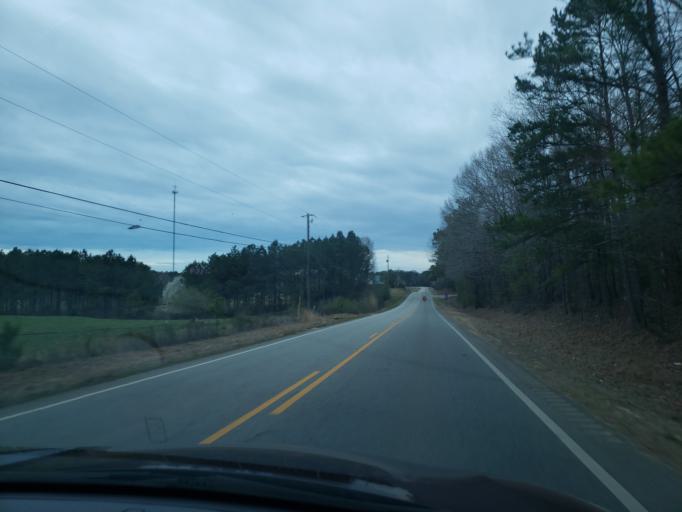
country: US
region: Alabama
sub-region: Chambers County
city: Lafayette
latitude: 32.9279
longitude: -85.3955
